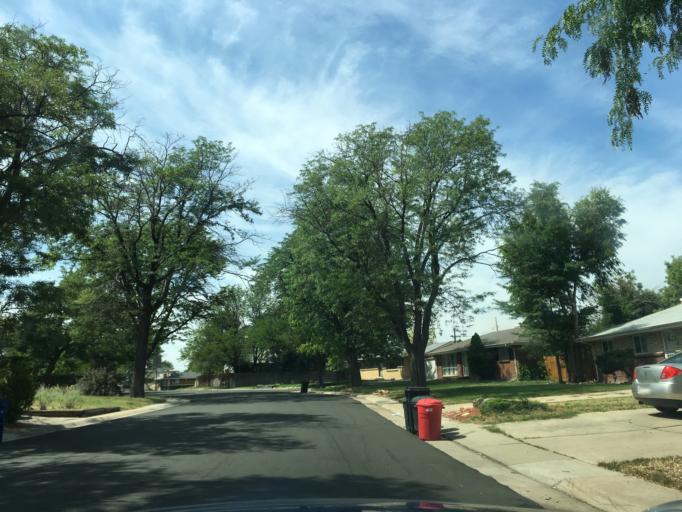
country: US
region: Colorado
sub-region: Adams County
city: Aurora
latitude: 39.7191
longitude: -104.8595
